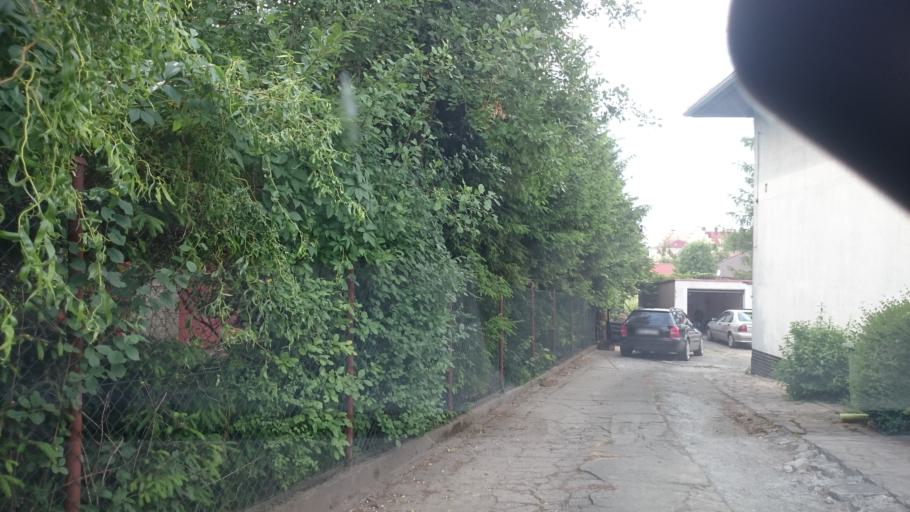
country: PL
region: Lower Silesian Voivodeship
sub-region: Powiat klodzki
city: Klodzko
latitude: 50.4537
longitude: 16.6629
